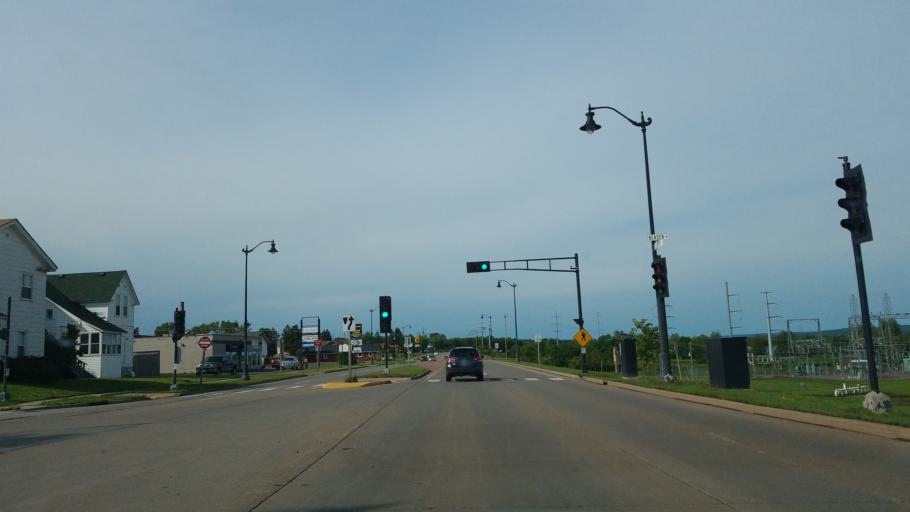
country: US
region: Wisconsin
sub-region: Ashland County
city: Ashland
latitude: 46.5861
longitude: -90.8986
